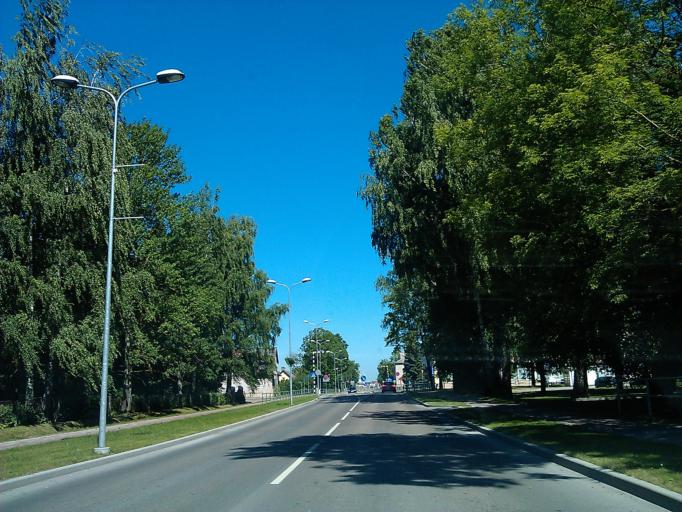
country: LV
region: Vilanu
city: Vilani
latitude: 56.5446
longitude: 26.9257
